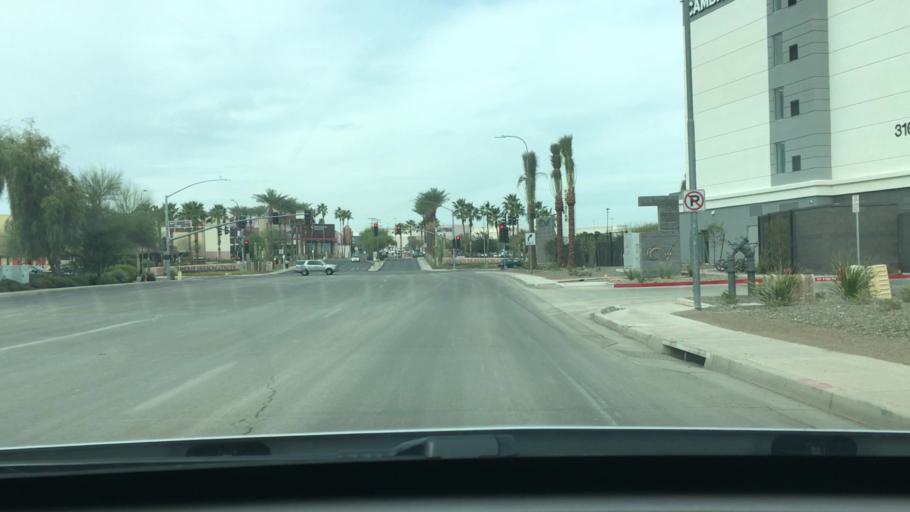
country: US
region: Arizona
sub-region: Maricopa County
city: Chandler
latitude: 33.2968
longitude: -111.8978
